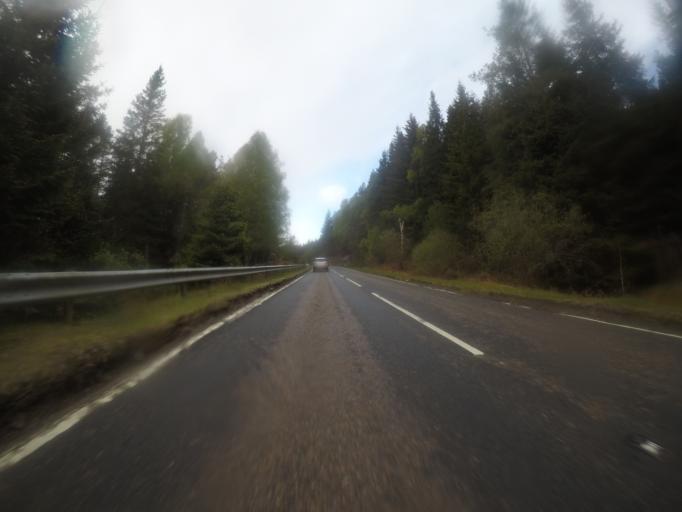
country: GB
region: Scotland
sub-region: Highland
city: Spean Bridge
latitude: 57.0826
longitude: -4.9262
